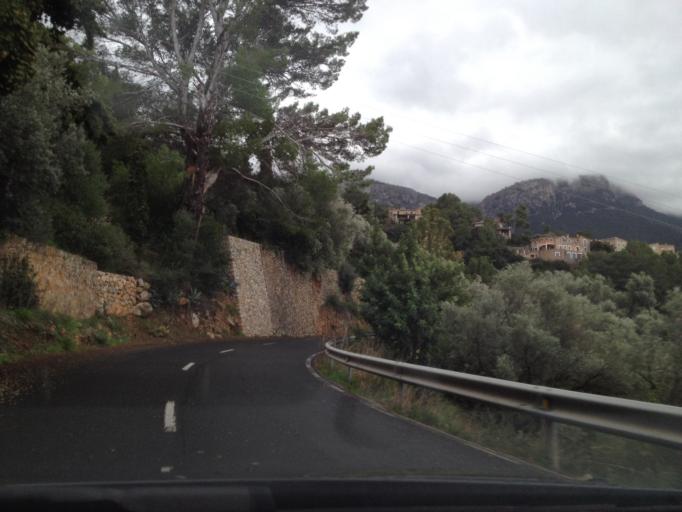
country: ES
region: Balearic Islands
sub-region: Illes Balears
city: Deia
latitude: 39.7597
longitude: 2.6505
